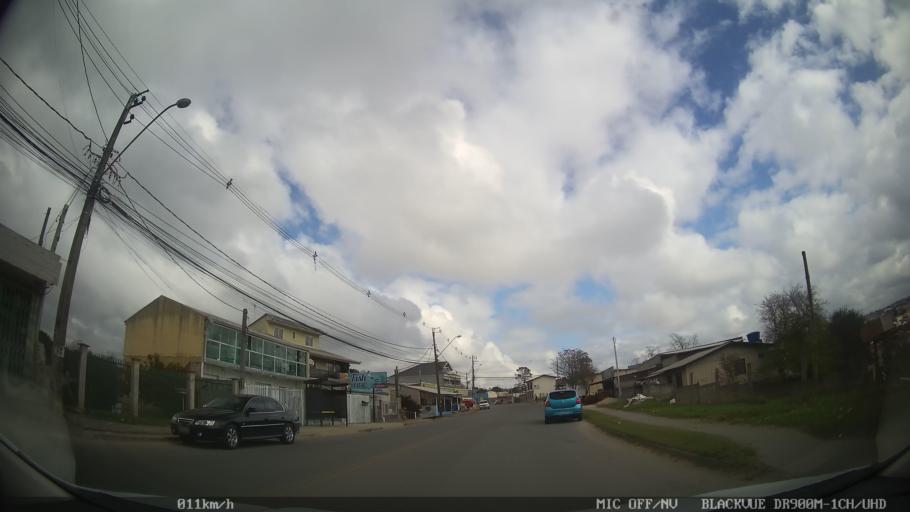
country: BR
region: Parana
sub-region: Colombo
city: Colombo
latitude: -25.3455
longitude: -49.2441
